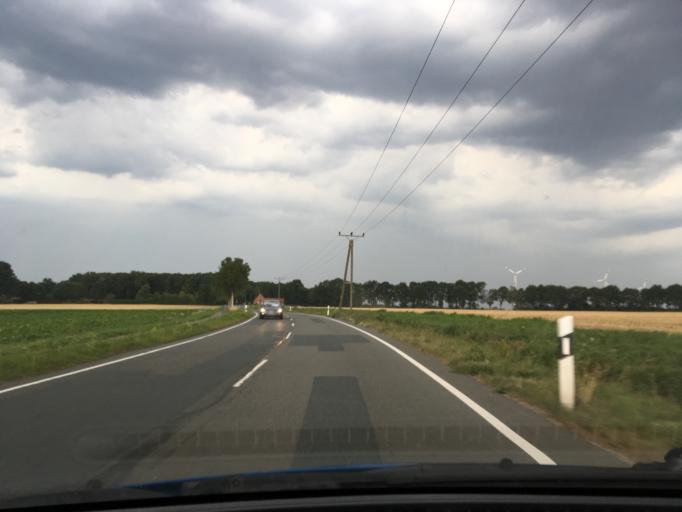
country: DE
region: Lower Saxony
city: Hanstedt Eins
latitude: 53.0451
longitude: 10.3580
